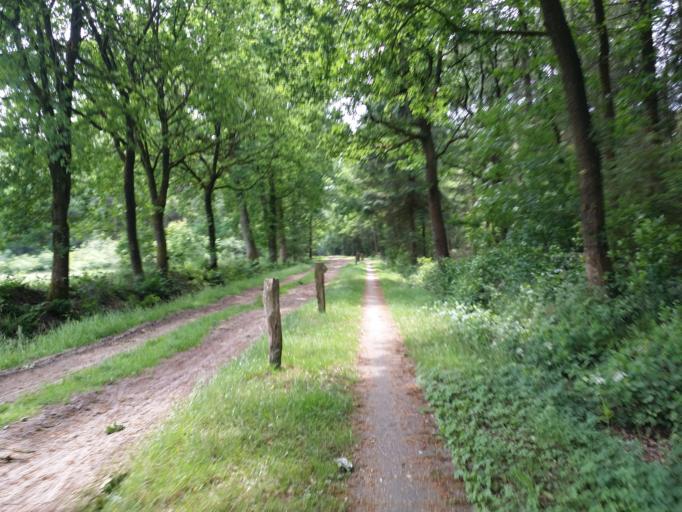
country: DE
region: Lower Saxony
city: Friedeburg
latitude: 53.4975
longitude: 7.8141
